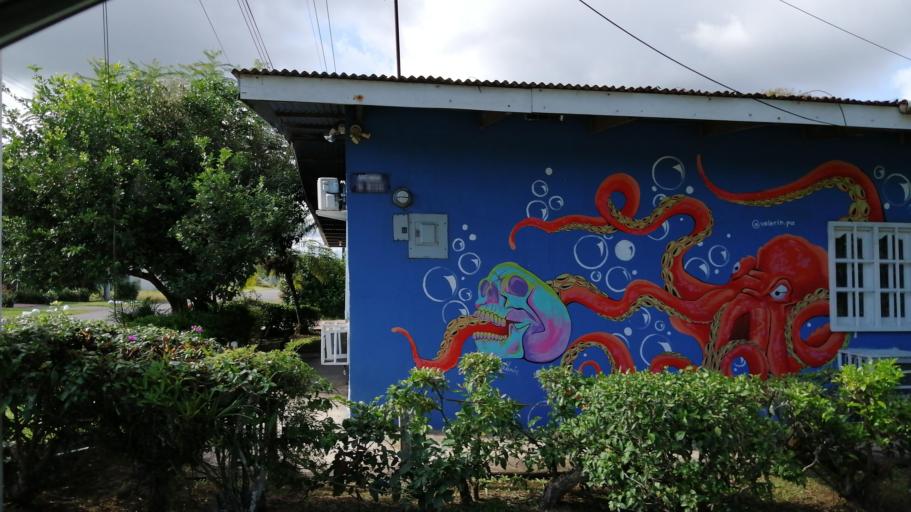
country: PA
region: Chiriqui
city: David
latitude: 8.4226
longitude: -82.4355
